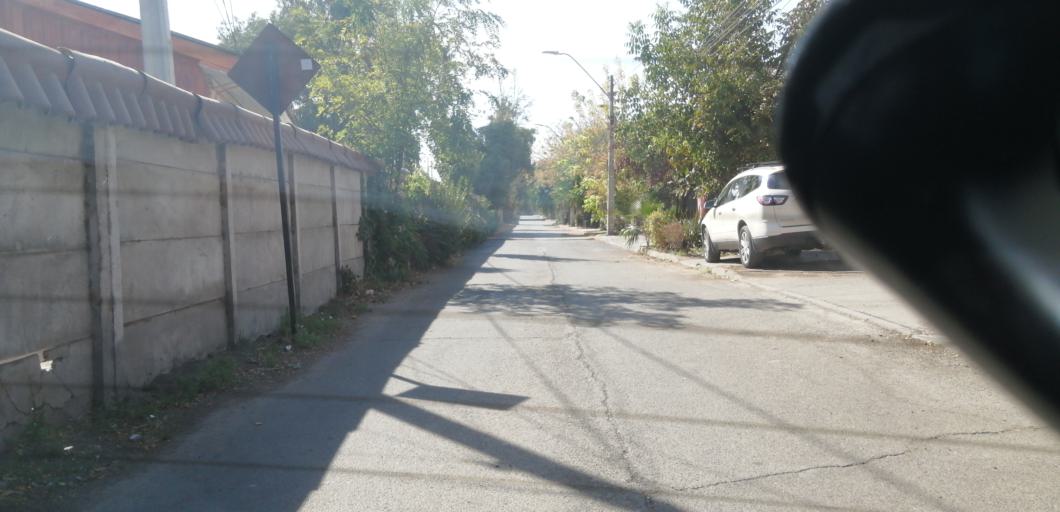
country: CL
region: Santiago Metropolitan
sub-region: Provincia de Santiago
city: Lo Prado
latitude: -33.4604
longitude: -70.7253
